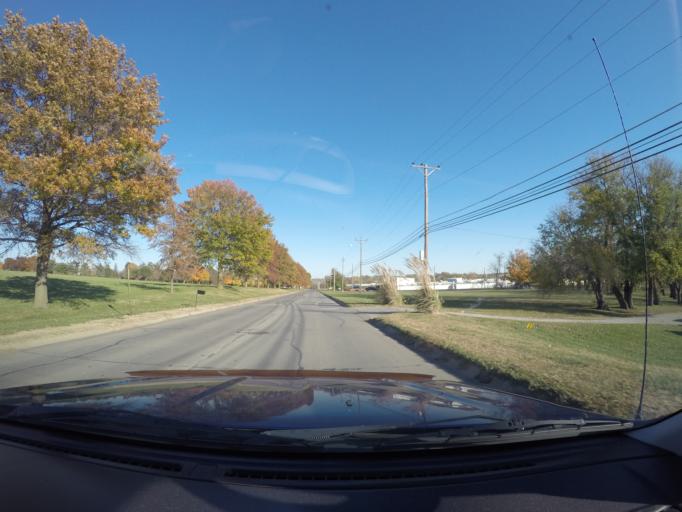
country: US
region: Nebraska
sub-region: Otoe County
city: Nebraska City
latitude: 40.6677
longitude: -95.8774
